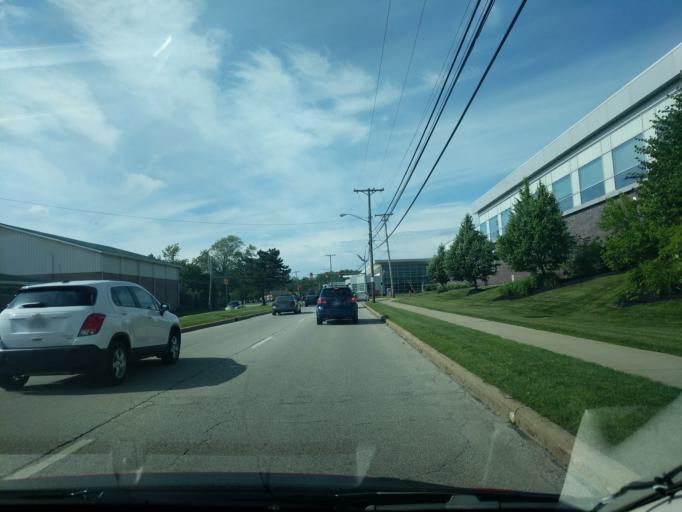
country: US
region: Ohio
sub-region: Cuyahoga County
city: North Randall
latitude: 41.4391
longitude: -81.5263
